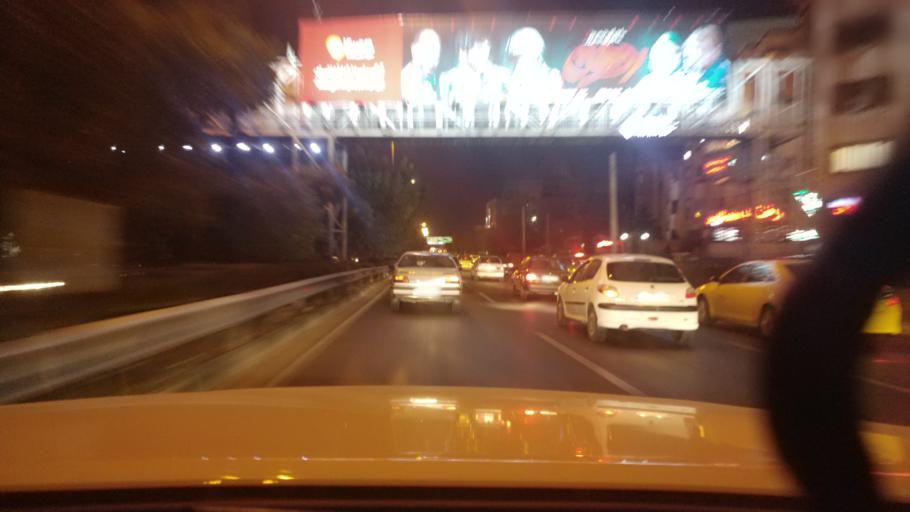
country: IR
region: Tehran
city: Tehran
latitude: 35.7386
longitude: 51.3265
